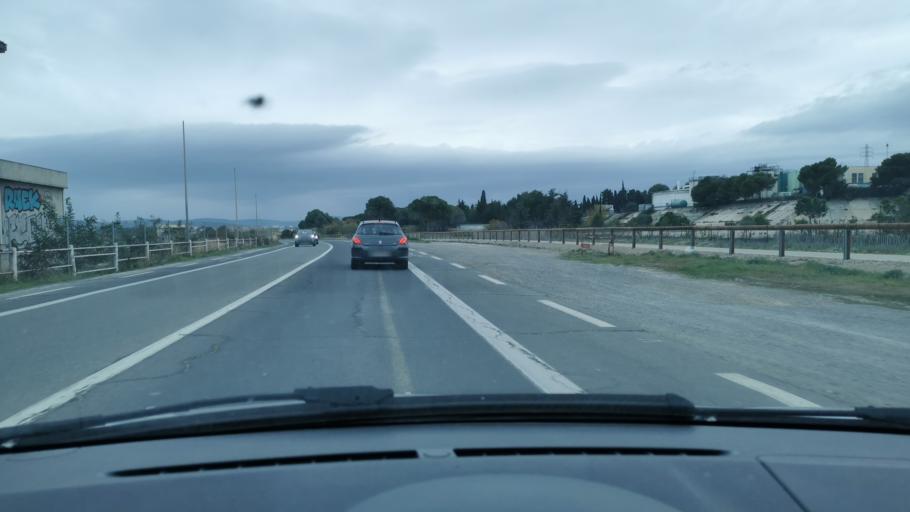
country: FR
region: Languedoc-Roussillon
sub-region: Departement de l'Herault
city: Sete
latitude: 43.4296
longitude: 3.7053
